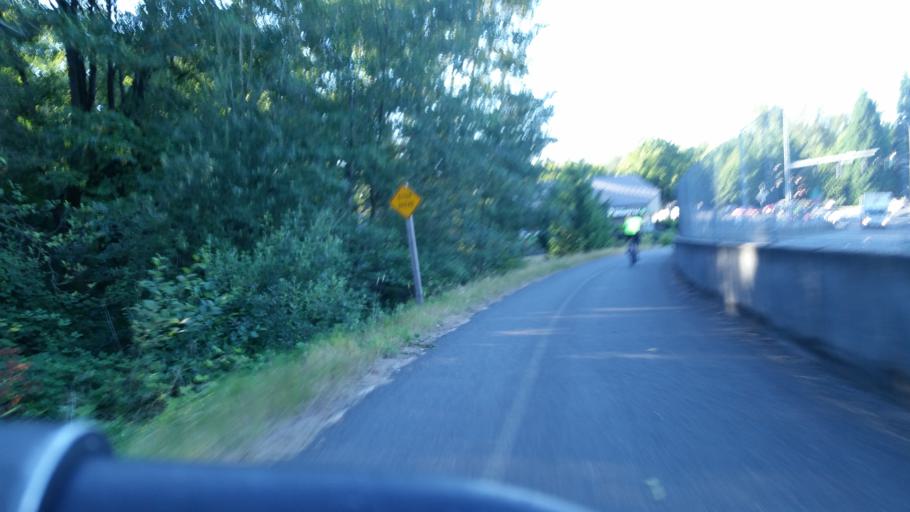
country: US
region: Washington
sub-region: King County
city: Redmond
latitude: 47.6685
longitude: -122.1299
